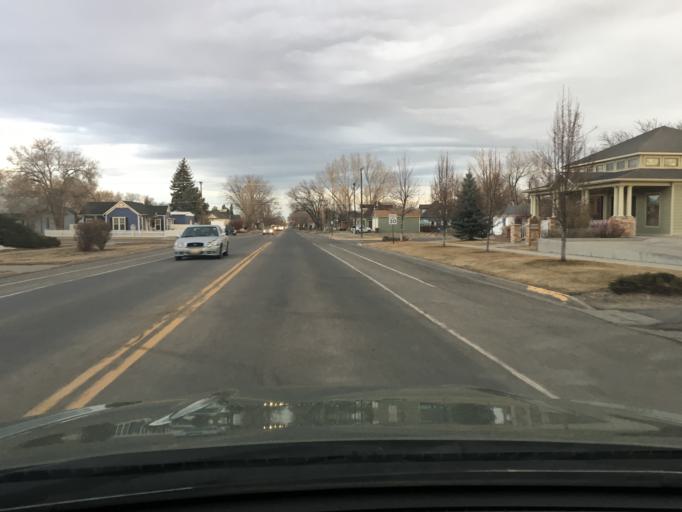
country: US
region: Colorado
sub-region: Montrose County
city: Montrose
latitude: 38.4774
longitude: -107.8707
